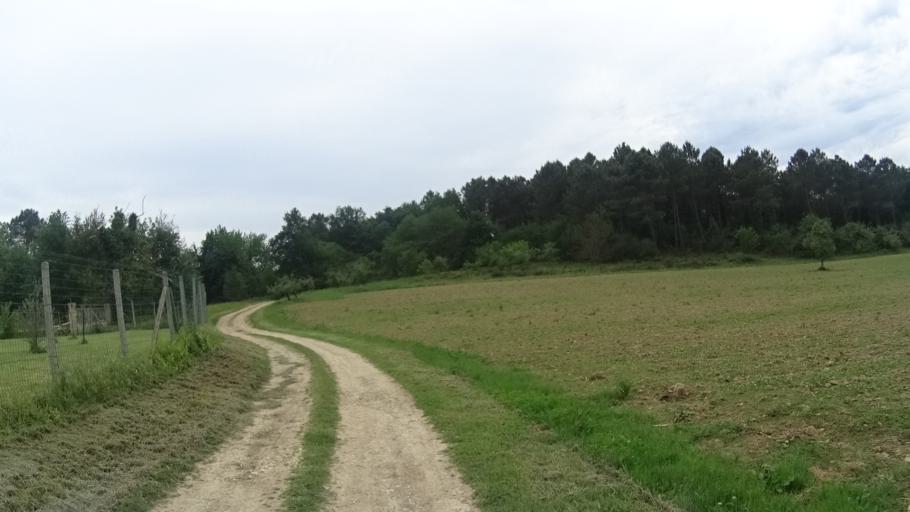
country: FR
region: Aquitaine
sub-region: Departement de la Dordogne
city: Sourzac
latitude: 44.9928
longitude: 0.4563
